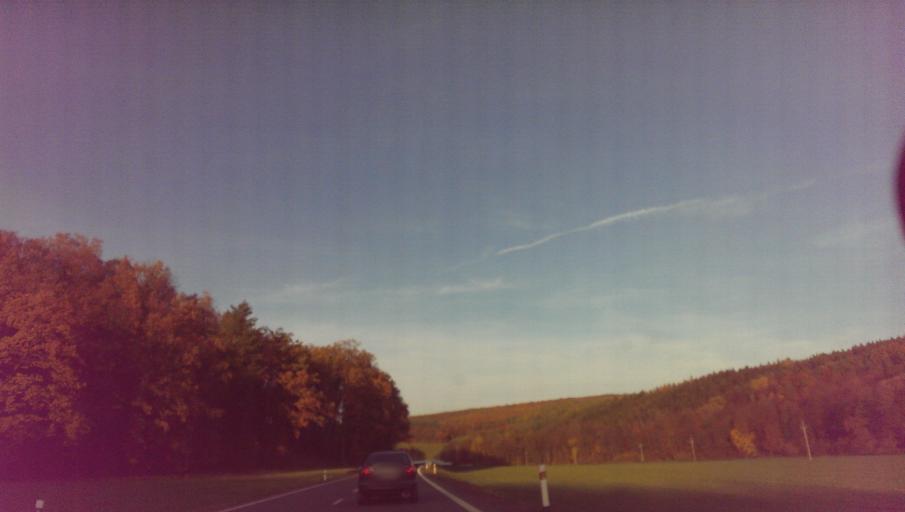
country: CZ
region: Zlin
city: Brezolupy
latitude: 49.1361
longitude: 17.6012
